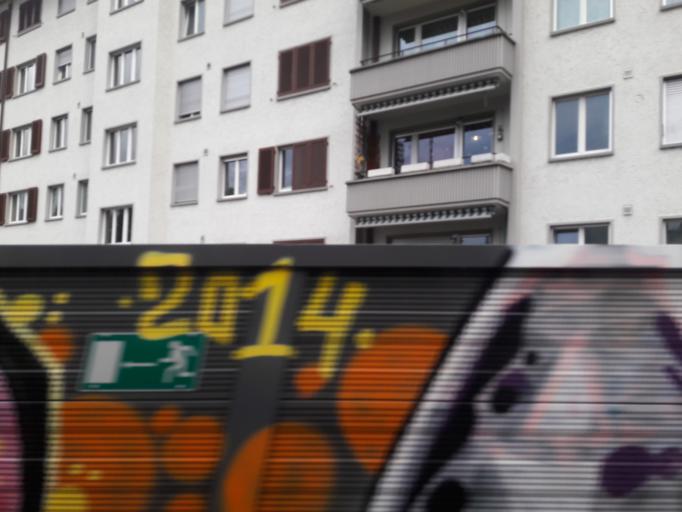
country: CH
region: Lucerne
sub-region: Lucerne-Stadt District
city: Luzern
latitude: 47.0525
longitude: 8.2969
